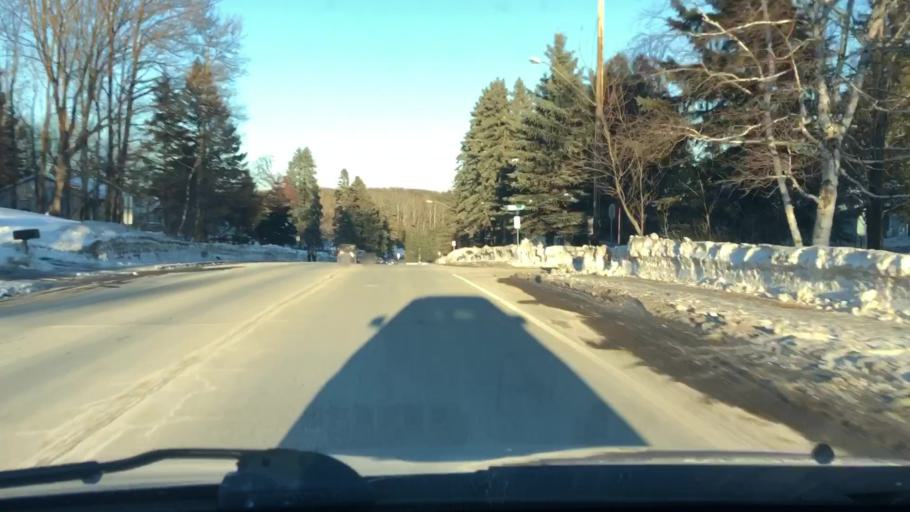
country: US
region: Minnesota
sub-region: Saint Louis County
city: Duluth
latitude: 46.8236
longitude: -92.0937
